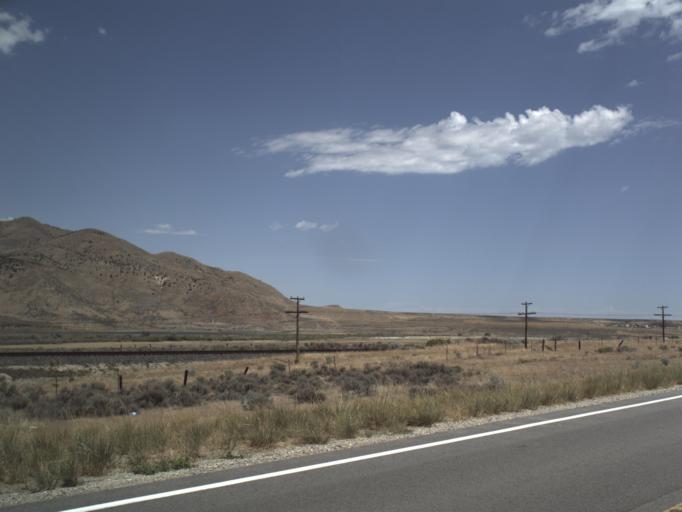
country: US
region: Utah
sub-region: Tooele County
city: Tooele
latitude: 40.4302
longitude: -112.3787
